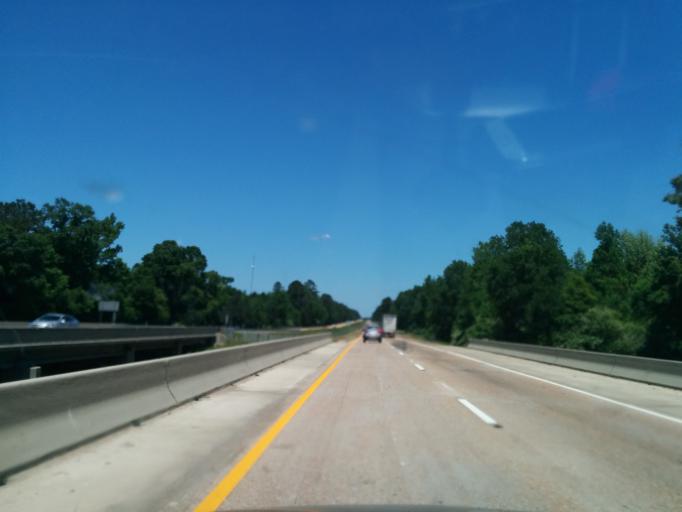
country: US
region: Mississippi
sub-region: Pike County
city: Magnolia
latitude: 31.1207
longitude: -90.4837
